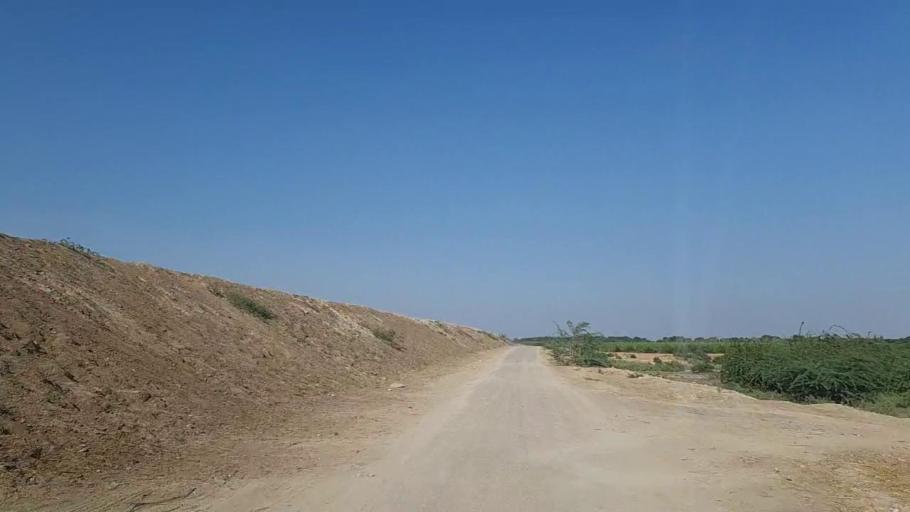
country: PK
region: Sindh
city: Chuhar Jamali
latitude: 24.5619
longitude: 68.0283
